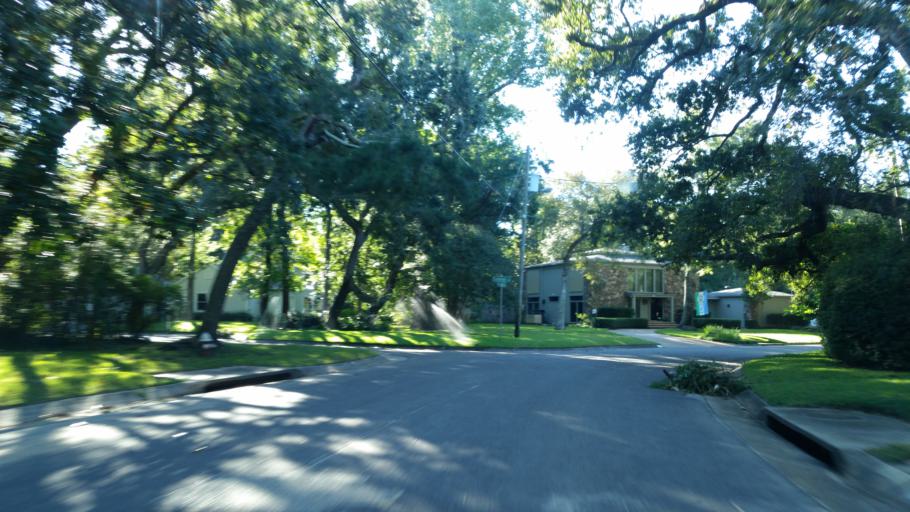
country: US
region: Florida
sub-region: Escambia County
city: East Pensacola Heights
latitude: 30.4692
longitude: -87.1647
